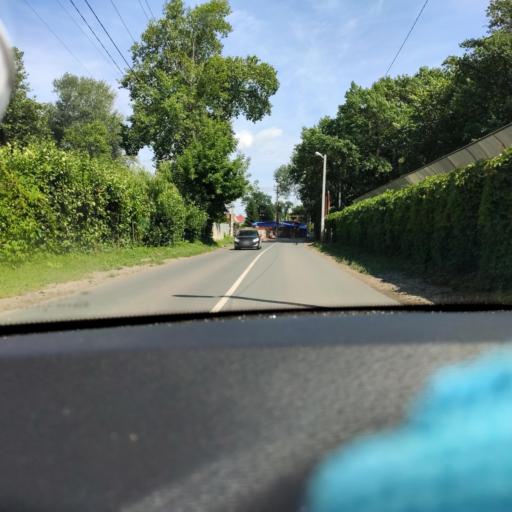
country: RU
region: Samara
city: Novokuybyshevsk
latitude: 53.1578
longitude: 49.9524
